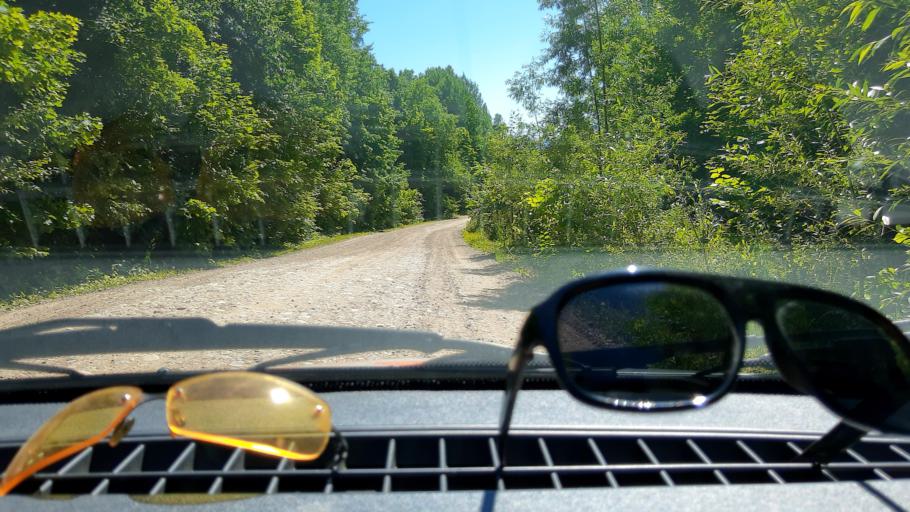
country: RU
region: Bashkortostan
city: Ulu-Telyak
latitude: 54.8053
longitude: 57.0356
